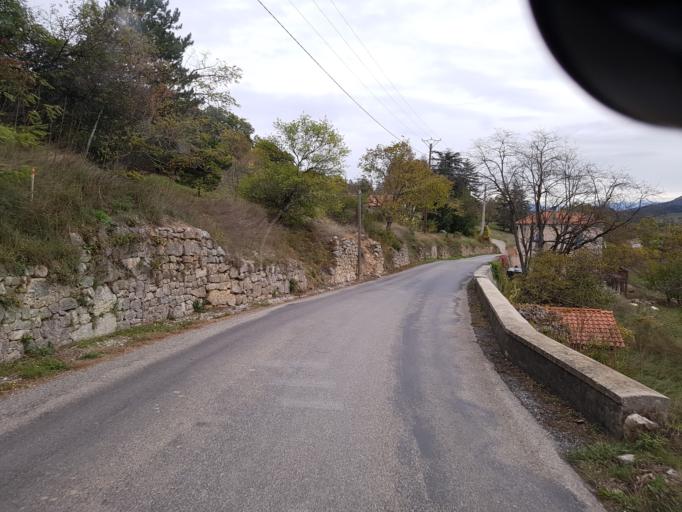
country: FR
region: Provence-Alpes-Cote d'Azur
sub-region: Departement des Hautes-Alpes
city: Laragne-Monteglin
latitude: 44.3154
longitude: 5.7065
